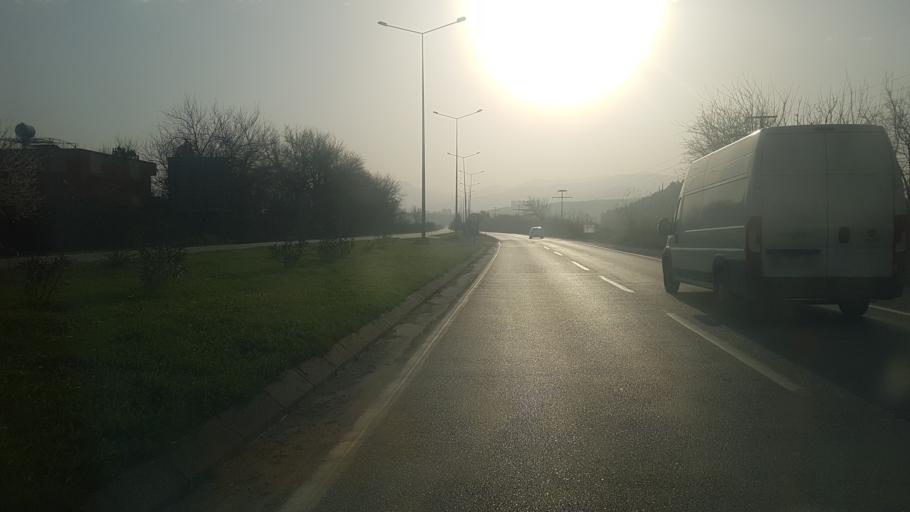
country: TR
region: Osmaniye
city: Toprakkale
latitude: 37.0560
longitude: 36.1250
